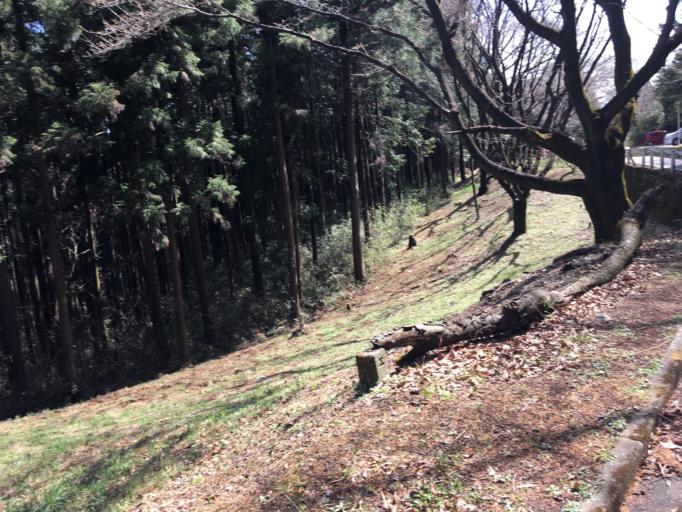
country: JP
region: Saitama
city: Ogawa
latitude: 36.0097
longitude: 139.3285
